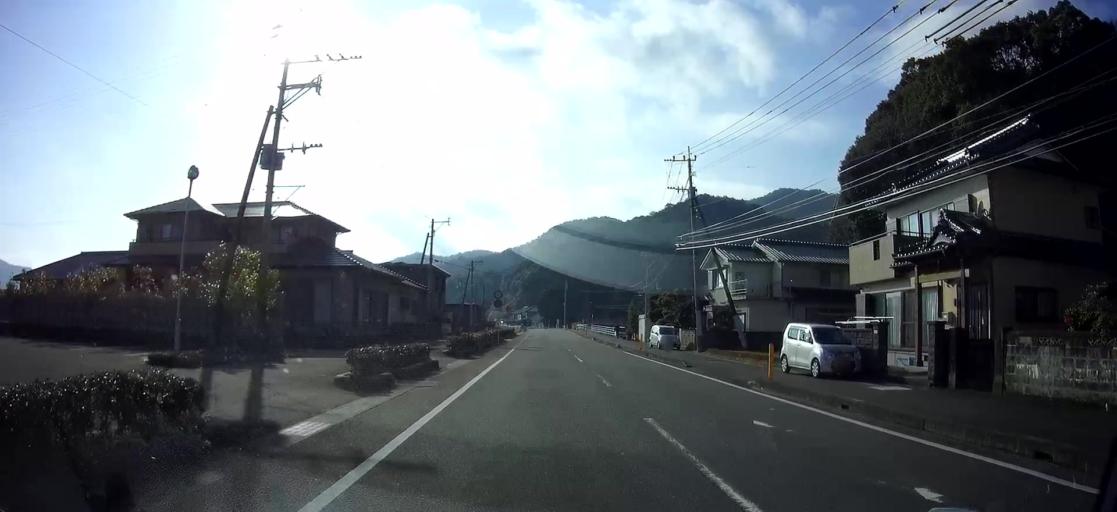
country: JP
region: Kumamoto
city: Yatsushiro
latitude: 32.4521
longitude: 130.4216
